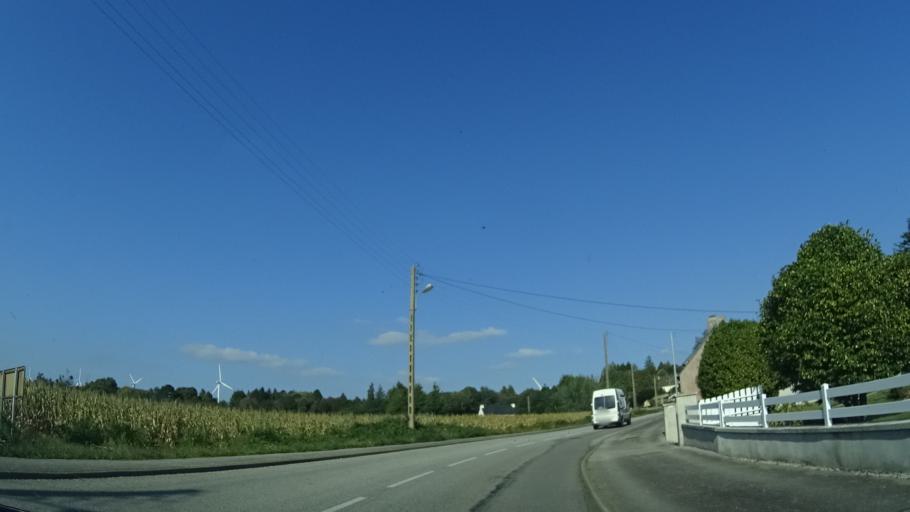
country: FR
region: Brittany
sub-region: Departement du Finistere
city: Cast
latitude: 48.1647
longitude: -4.1292
